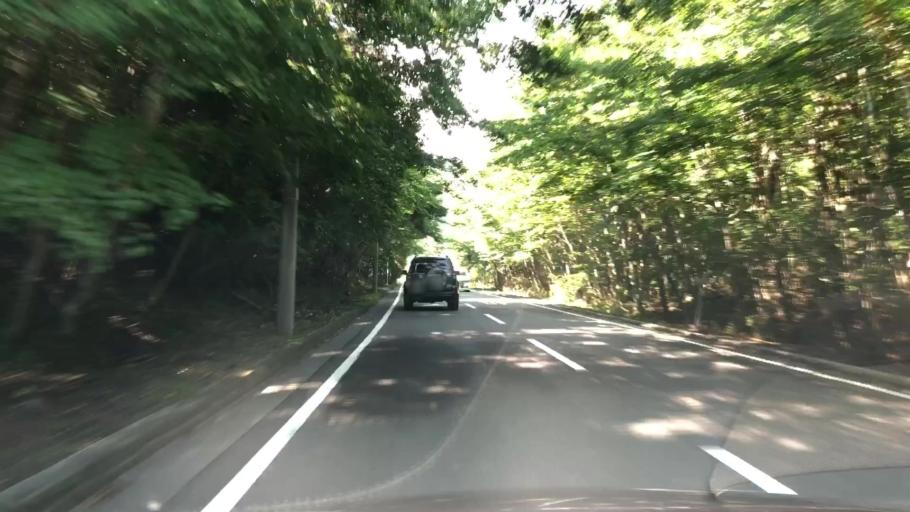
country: JP
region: Shizuoka
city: Gotemba
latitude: 35.3159
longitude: 138.7871
